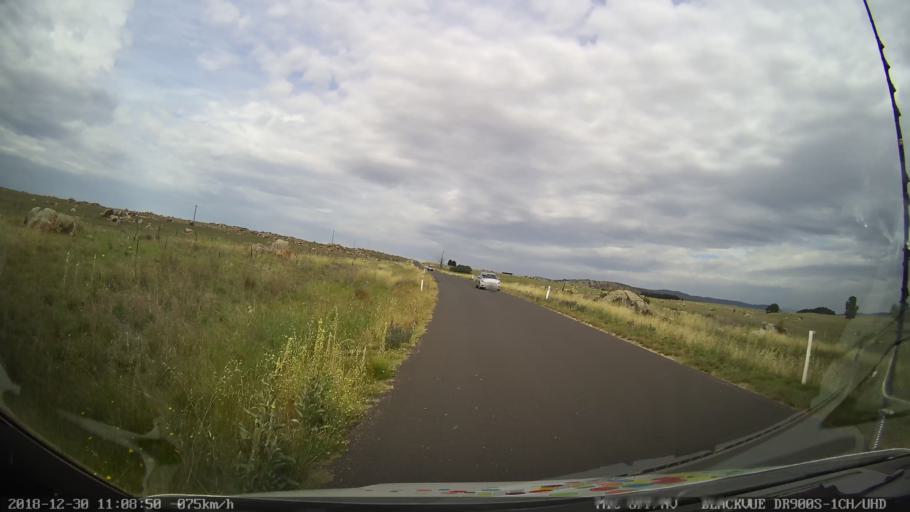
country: AU
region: New South Wales
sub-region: Snowy River
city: Berridale
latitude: -36.5042
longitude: 148.8013
